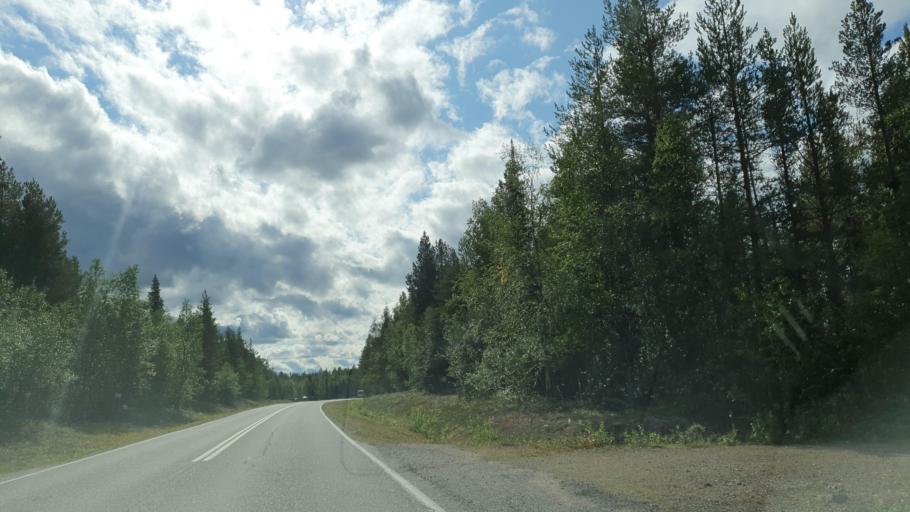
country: FI
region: Lapland
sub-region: Tunturi-Lappi
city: Muonio
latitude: 67.8786
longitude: 24.2070
